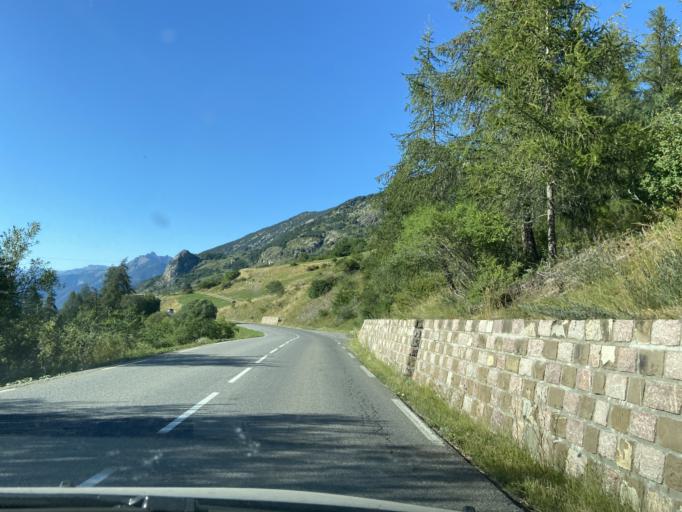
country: FR
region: Provence-Alpes-Cote d'Azur
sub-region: Departement des Hautes-Alpes
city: Guillestre
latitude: 44.5990
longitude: 6.6899
